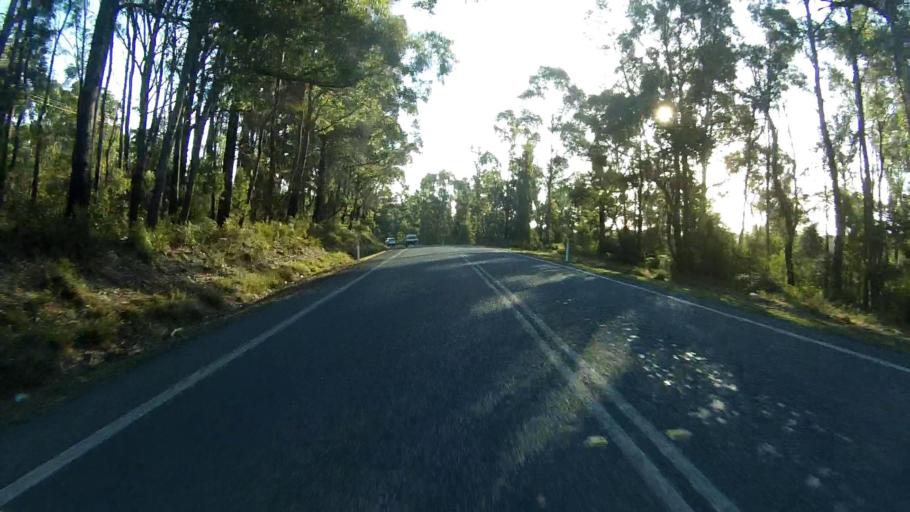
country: AU
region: Tasmania
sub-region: Sorell
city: Sorell
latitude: -42.9671
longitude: 147.8994
